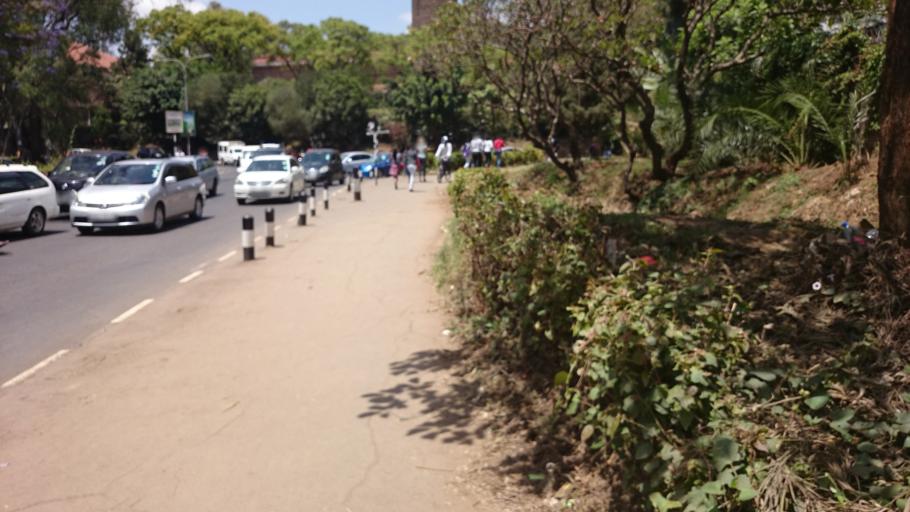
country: KE
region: Nairobi Area
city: Nairobi
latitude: -1.2818
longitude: 36.8146
